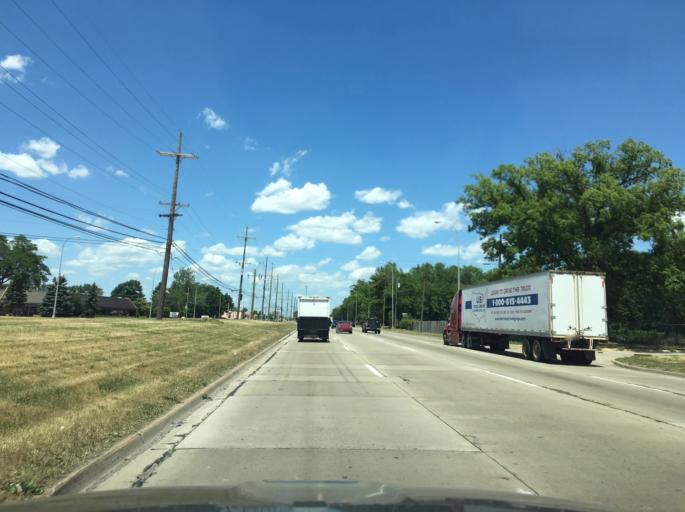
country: US
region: Michigan
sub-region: Macomb County
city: Center Line
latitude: 42.5015
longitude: -83.0462
